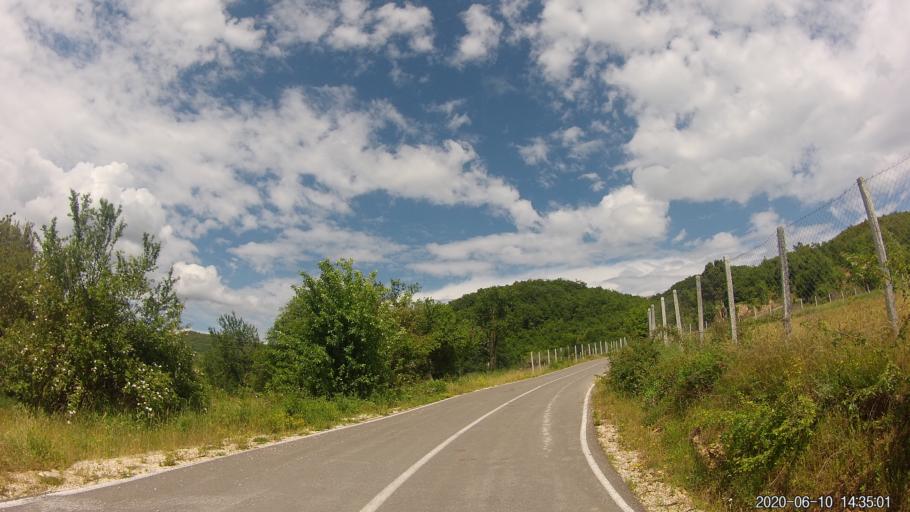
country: XK
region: Prizren
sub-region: Komuna e Therandes
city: Budakovo
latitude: 42.4136
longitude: 20.9328
